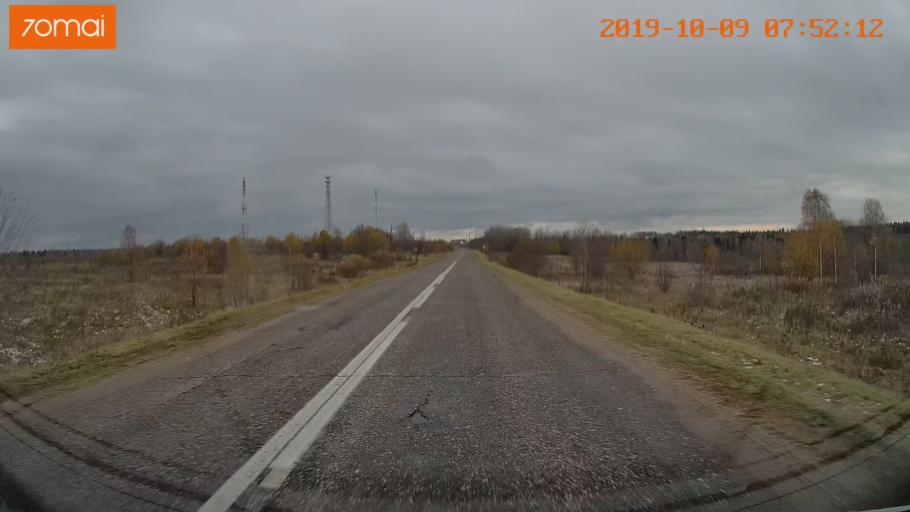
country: RU
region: Jaroslavl
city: Kukoboy
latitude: 58.6891
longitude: 39.8835
